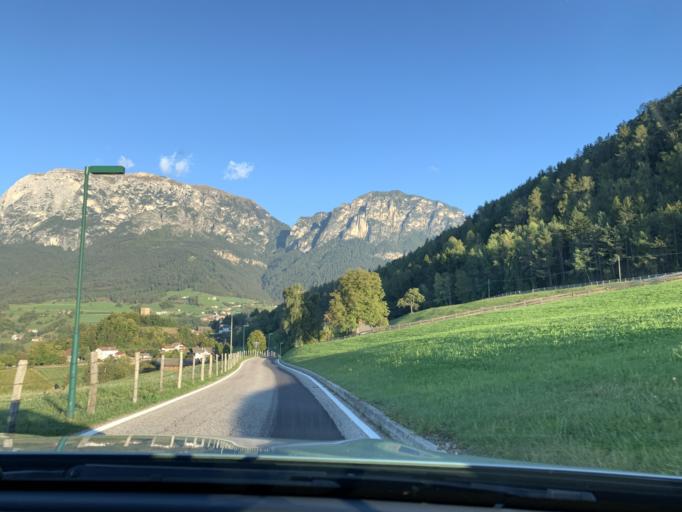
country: IT
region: Trentino-Alto Adige
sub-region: Bolzano
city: Fie Allo Sciliar
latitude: 46.5033
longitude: 11.4889
